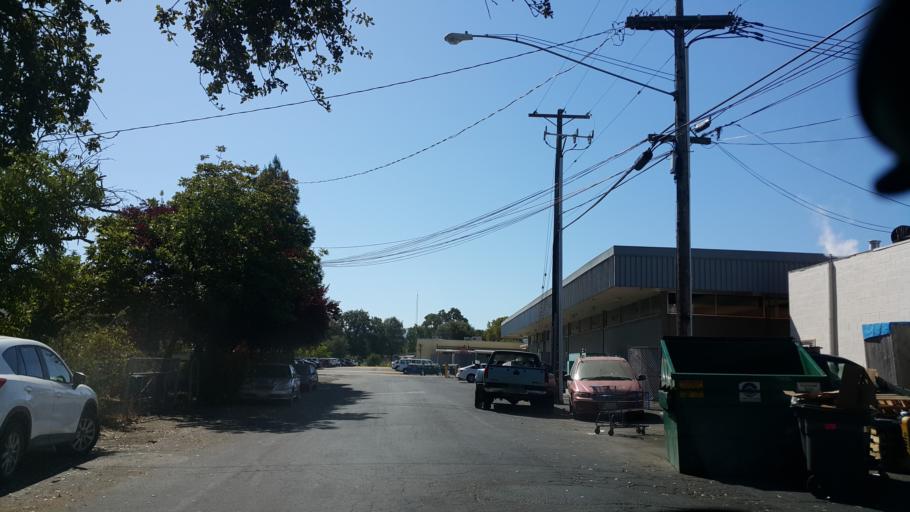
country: US
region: California
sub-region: Mendocino County
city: Ukiah
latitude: 39.1431
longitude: -123.2047
